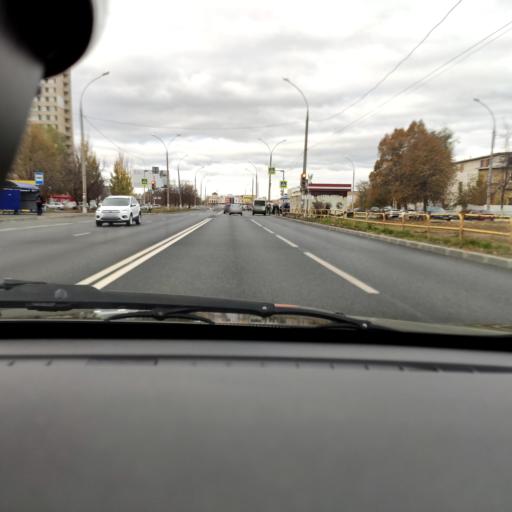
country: RU
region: Samara
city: Tol'yatti
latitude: 53.5431
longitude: 49.3226
